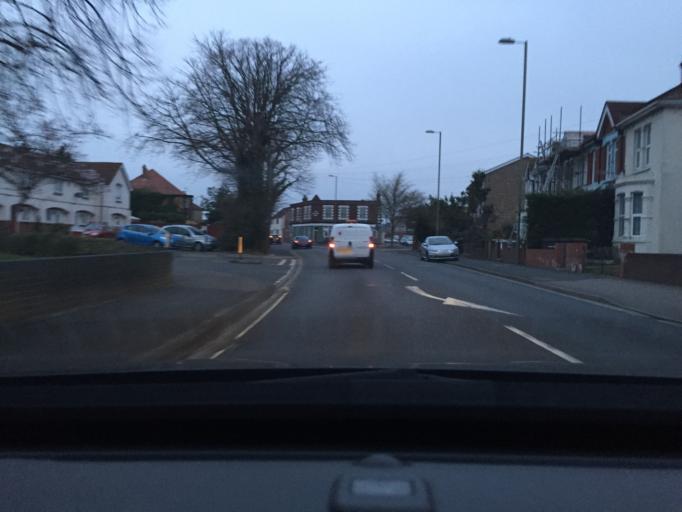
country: GB
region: England
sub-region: Hampshire
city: Gosport
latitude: 50.8096
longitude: -1.1533
